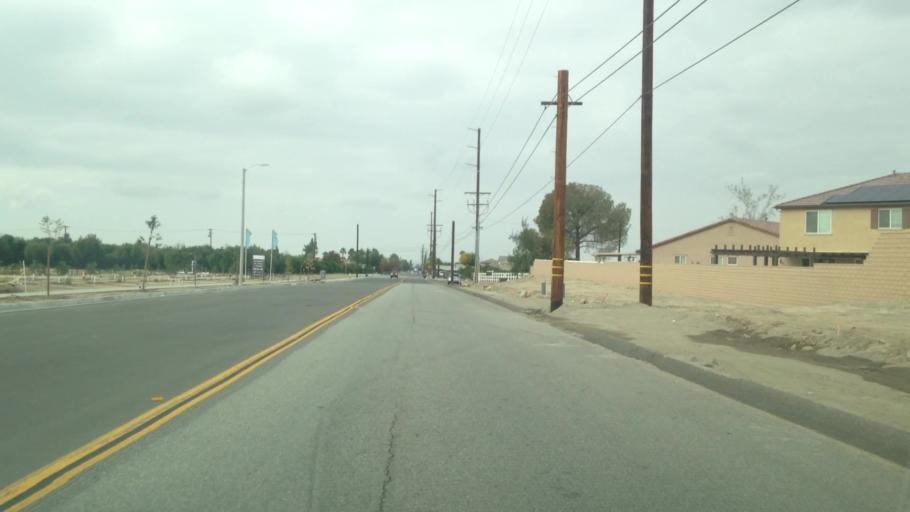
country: US
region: California
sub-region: San Bernardino County
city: Mentone
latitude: 34.0773
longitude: -117.1526
